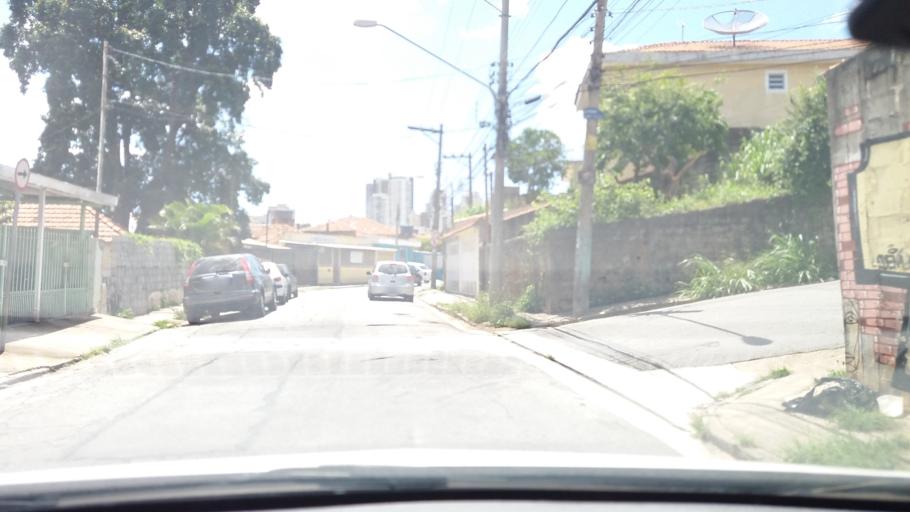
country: BR
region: Sao Paulo
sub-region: Sao Paulo
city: Sao Paulo
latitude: -23.4804
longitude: -46.6250
